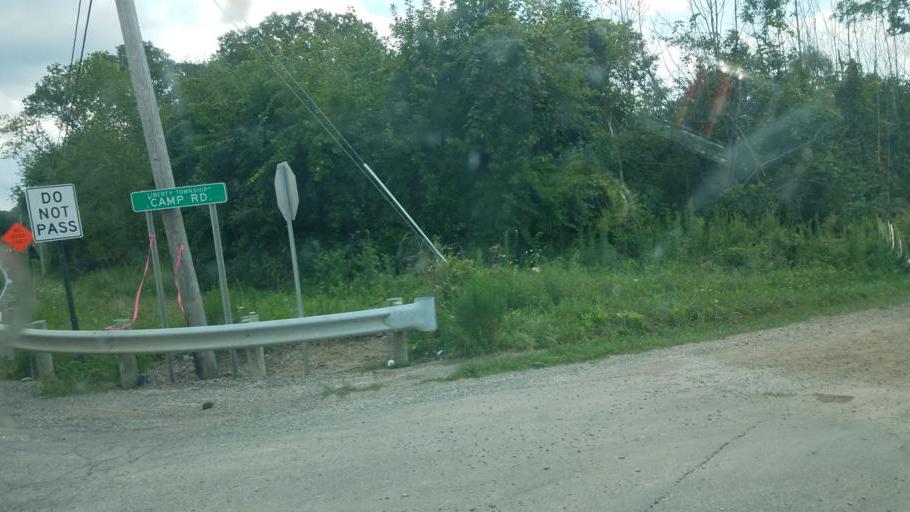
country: US
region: Ohio
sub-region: Knox County
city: Centerburg
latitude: 40.4044
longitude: -82.6321
